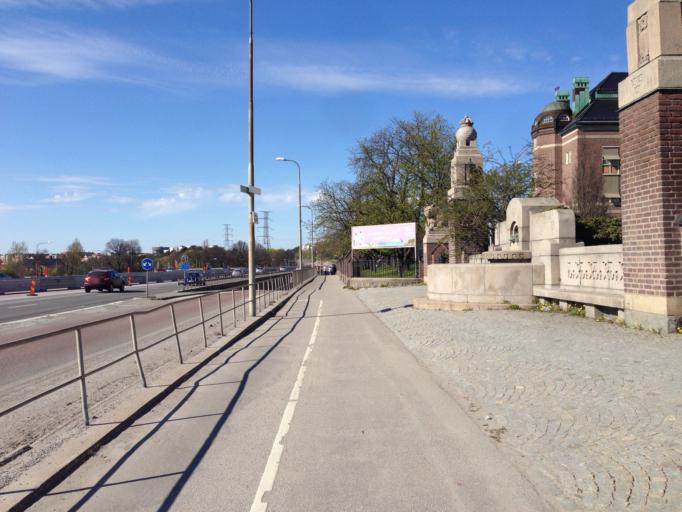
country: SE
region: Stockholm
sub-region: Norrtalje Kommun
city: Bergshamra
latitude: 59.3684
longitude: 18.0521
